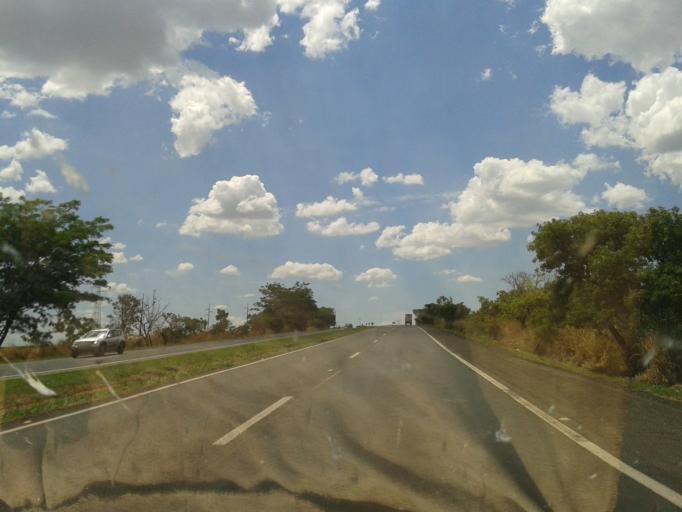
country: BR
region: Minas Gerais
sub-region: Uberlandia
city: Uberlandia
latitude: -19.0844
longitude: -48.1861
